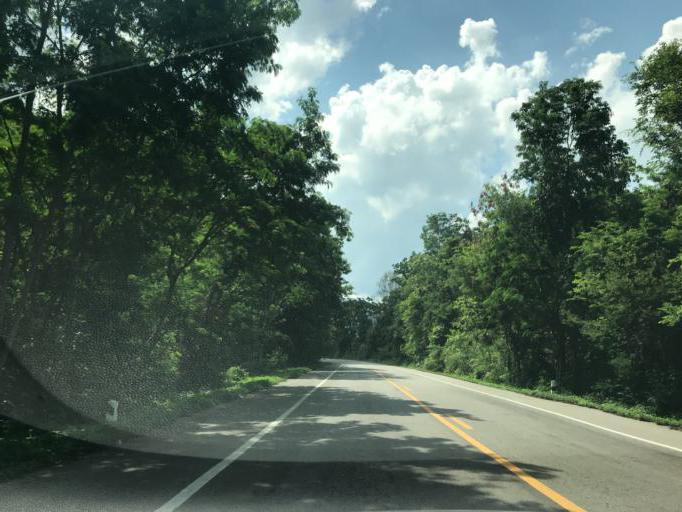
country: TH
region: Phayao
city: Phayao
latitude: 19.0880
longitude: 99.8143
